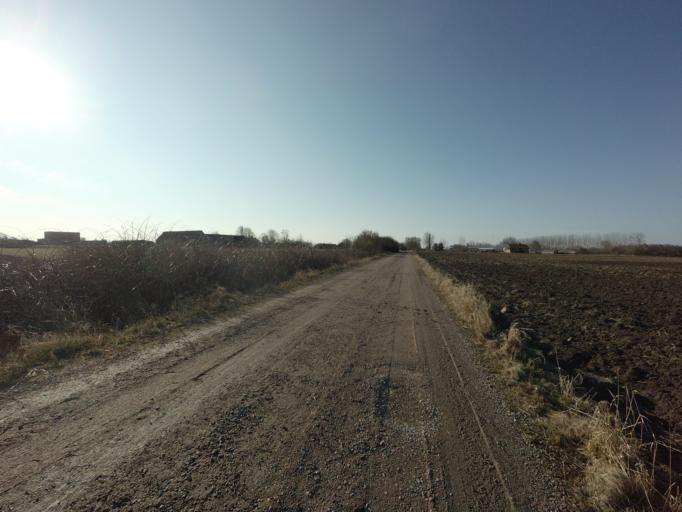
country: SE
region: Skane
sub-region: Hoganas Kommun
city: Hoganas
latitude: 56.1488
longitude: 12.5922
